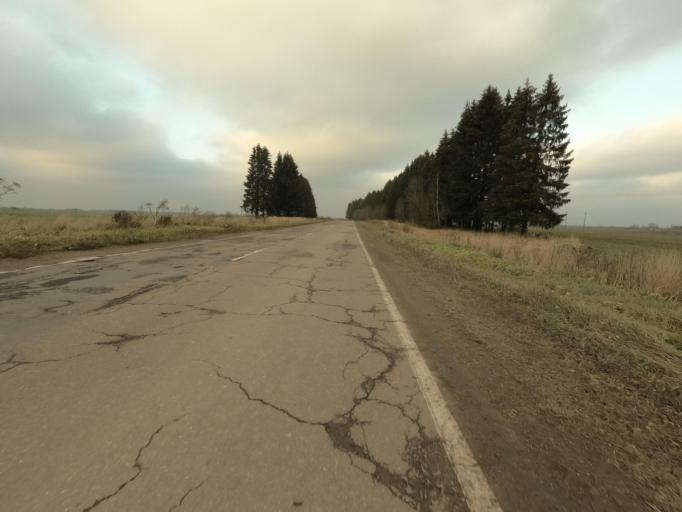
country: RU
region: Leningrad
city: Mga
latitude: 59.7780
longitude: 31.0245
